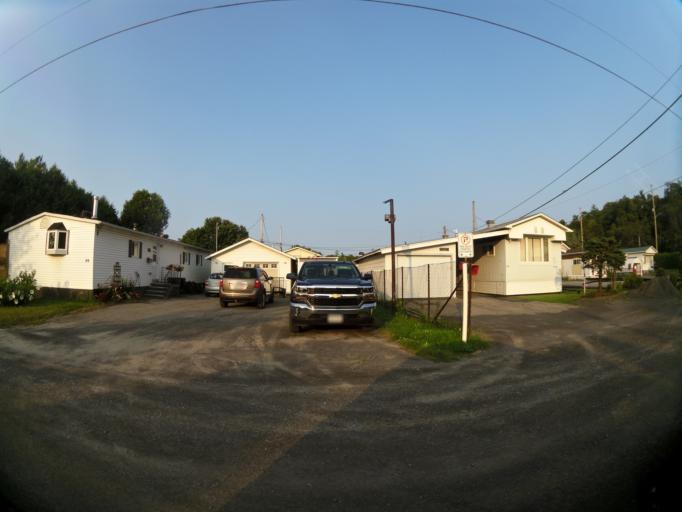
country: CA
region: Quebec
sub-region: Outaouais
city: Gatineau
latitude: 45.4873
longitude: -75.4938
